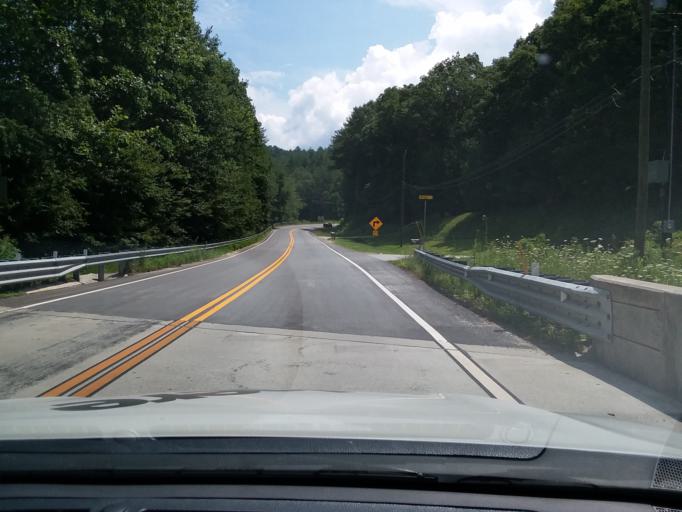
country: US
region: Georgia
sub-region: Rabun County
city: Mountain City
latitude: 34.9849
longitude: -83.3819
